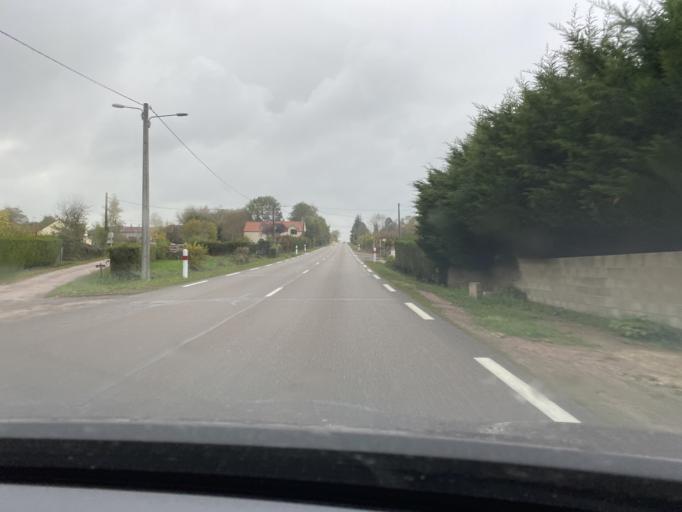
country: FR
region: Bourgogne
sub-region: Departement de la Cote-d'Or
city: Saulieu
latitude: 47.2914
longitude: 4.2203
